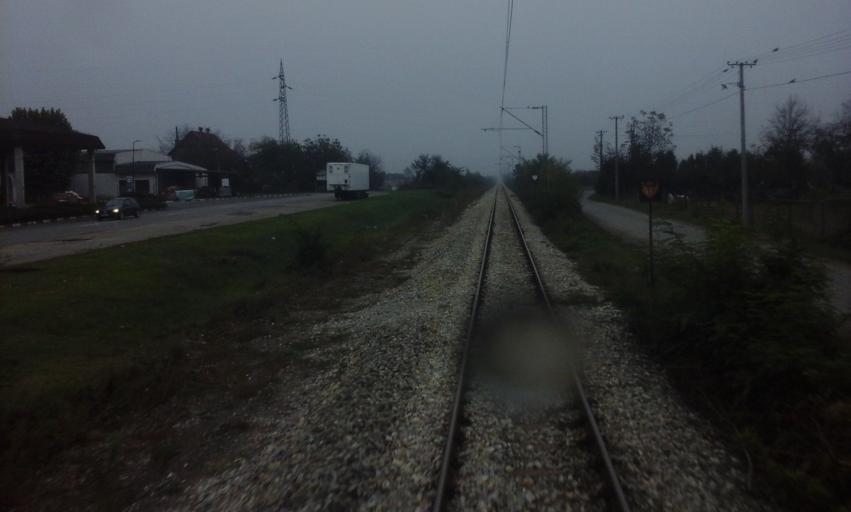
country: RS
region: Central Serbia
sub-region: Pomoravski Okrug
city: Cuprija
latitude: 43.9033
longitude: 21.3788
